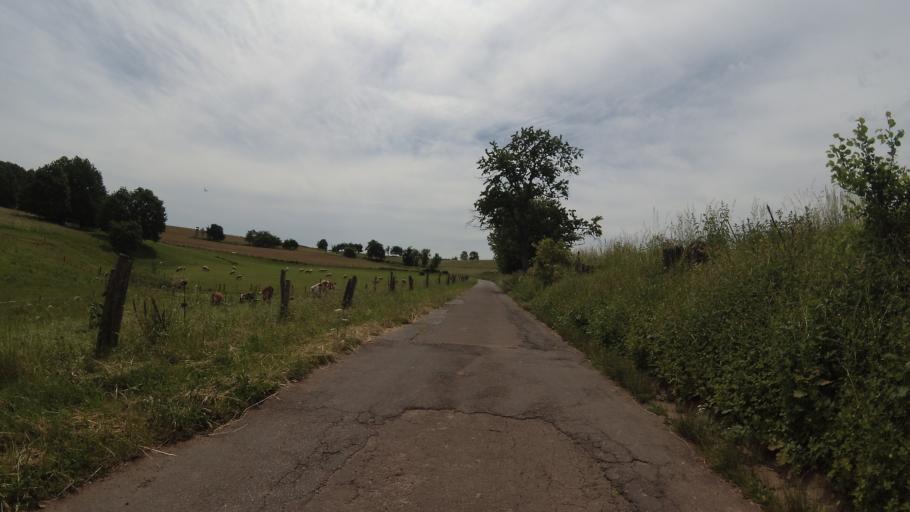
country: DE
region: Saarland
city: Ottweiler
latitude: 49.4268
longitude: 7.1746
